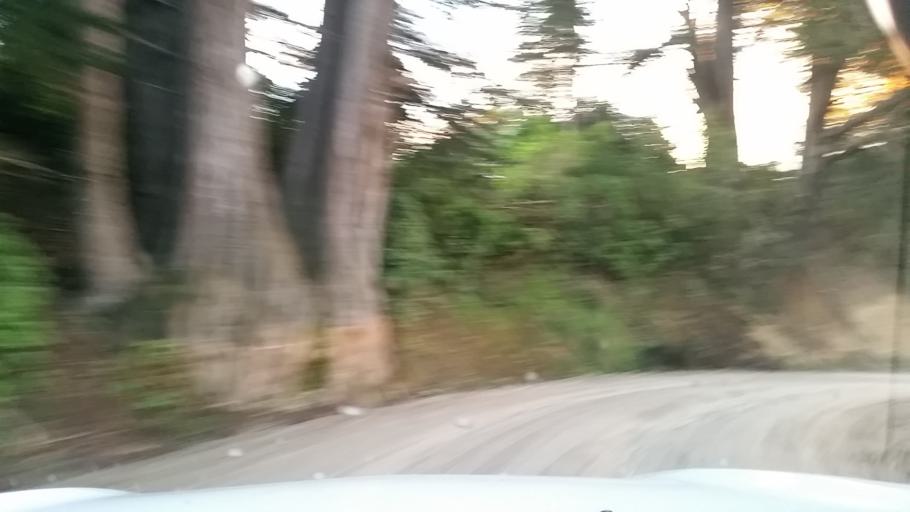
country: NZ
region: Manawatu-Wanganui
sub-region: Wanganui District
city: Wanganui
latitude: -39.7682
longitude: 174.8713
